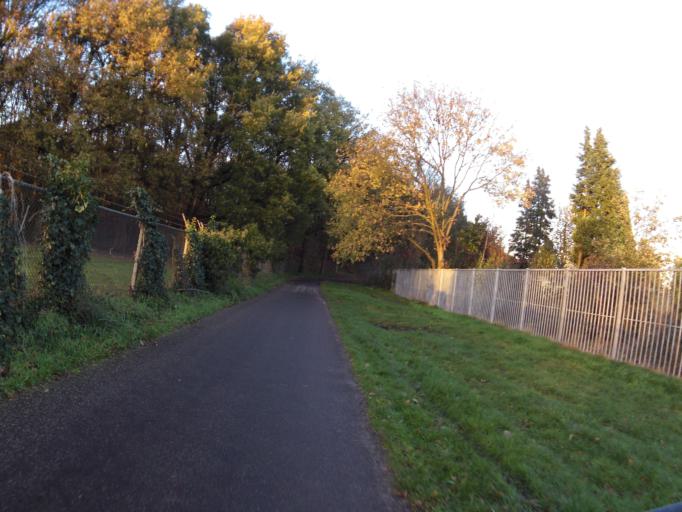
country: NL
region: North Brabant
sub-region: Gemeente Loon op Zand
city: Loon op Zand
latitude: 51.6357
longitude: 5.1136
